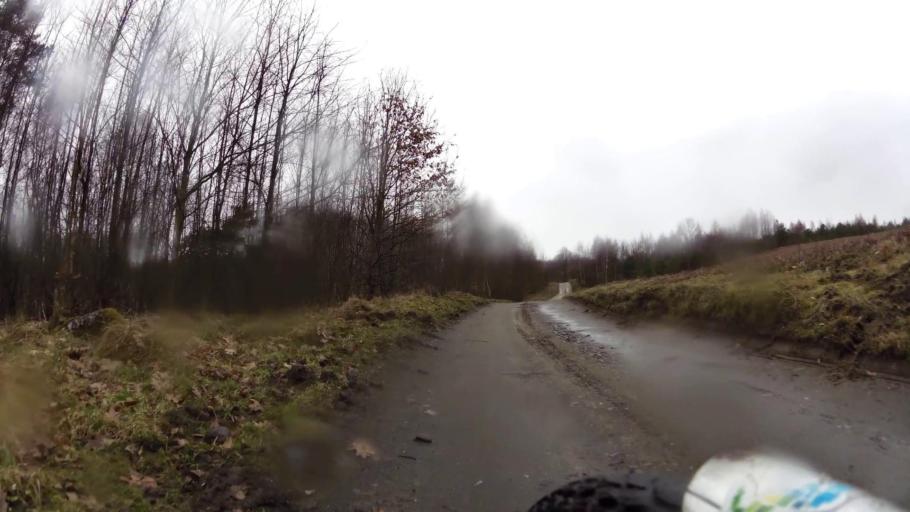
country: PL
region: Pomeranian Voivodeship
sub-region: Powiat bytowski
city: Miastko
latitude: 54.0440
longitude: 17.0492
